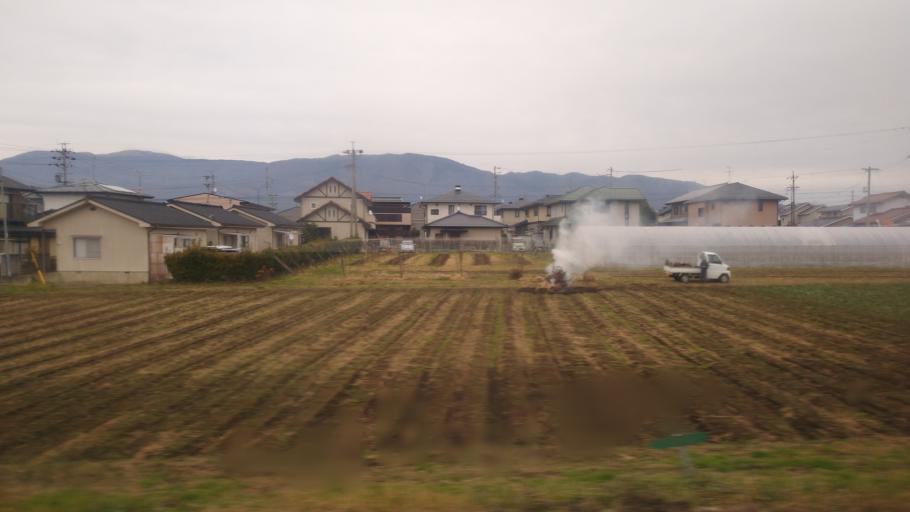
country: JP
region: Nagano
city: Shiojiri
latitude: 36.1258
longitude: 137.9484
